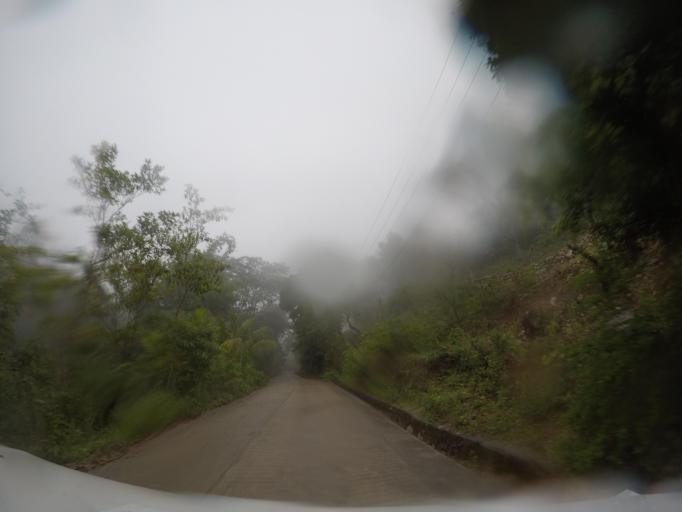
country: TL
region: Baucau
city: Venilale
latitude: -8.6334
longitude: 126.4218
